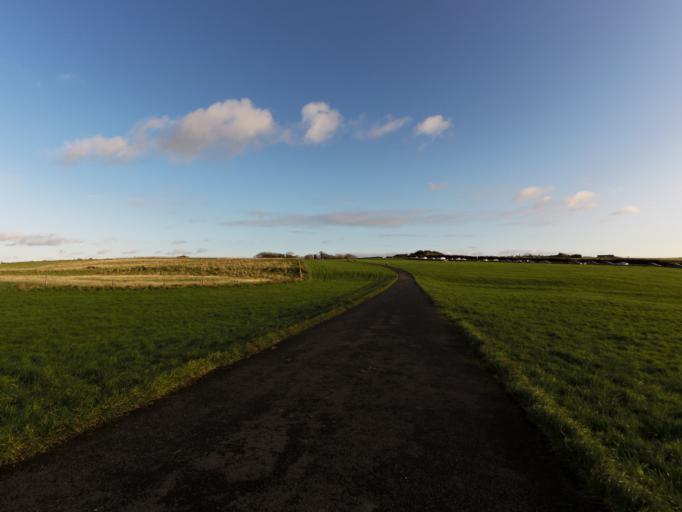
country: IE
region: Connaught
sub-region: County Galway
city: Oranmore
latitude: 53.2467
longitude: -8.9610
